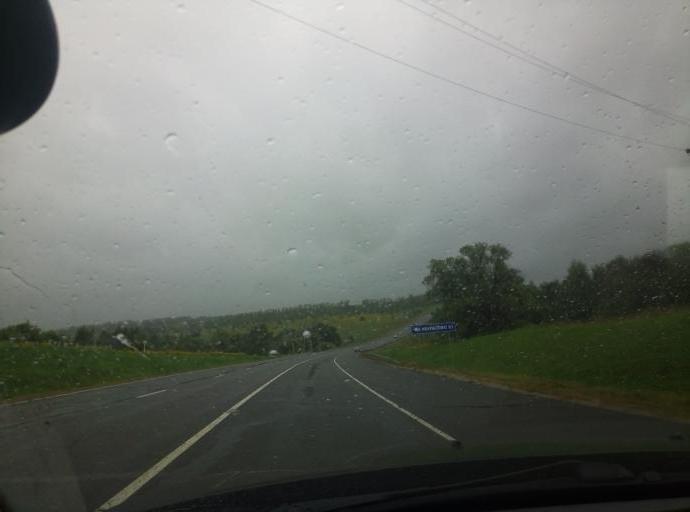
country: RU
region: Tula
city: Barsuki
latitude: 54.2939
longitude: 37.5354
